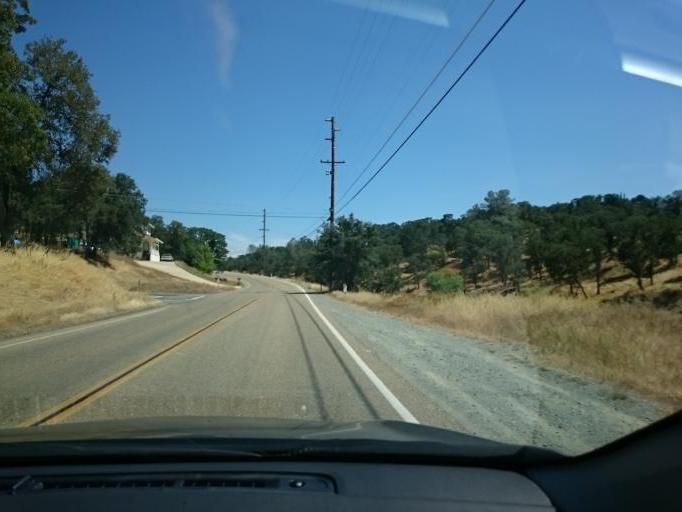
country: US
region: California
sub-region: Calaveras County
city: Rancho Calaveras
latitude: 38.1558
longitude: -120.8384
